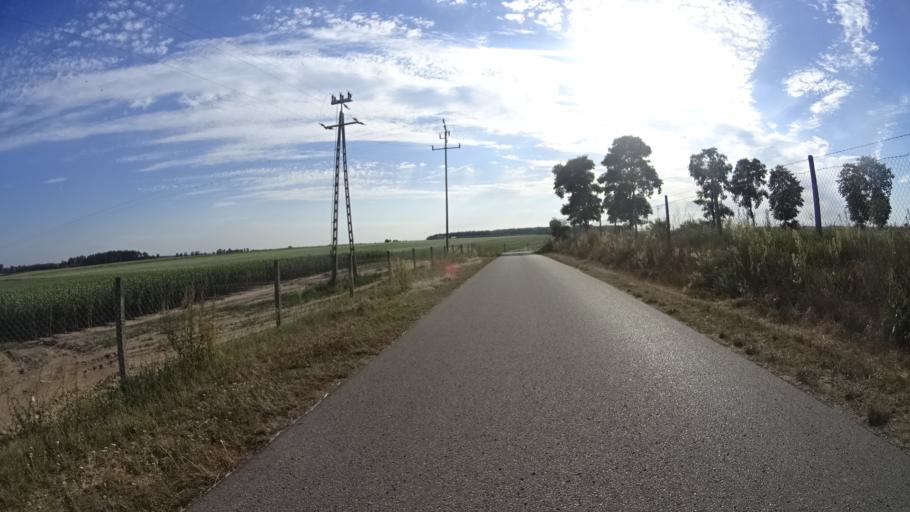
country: PL
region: Masovian Voivodeship
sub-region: Powiat grojecki
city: Goszczyn
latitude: 51.6817
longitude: 20.8267
